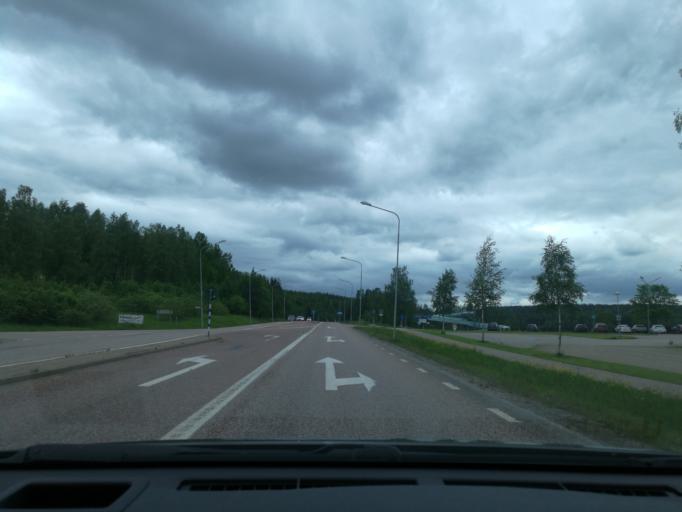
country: SE
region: Vaestmanland
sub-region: Fagersta Kommun
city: Fagersta
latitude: 59.9799
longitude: 15.7957
